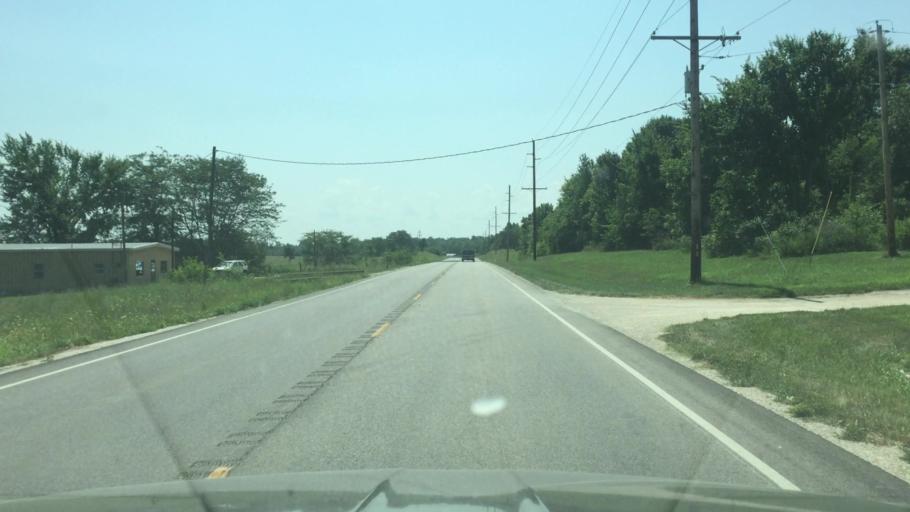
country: US
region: Missouri
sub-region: Miller County
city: Eldon
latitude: 38.3850
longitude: -92.6881
